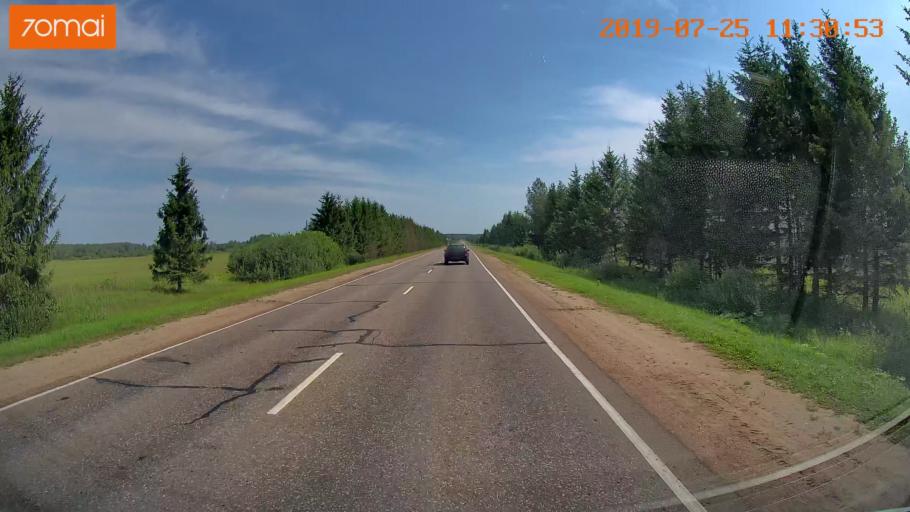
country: RU
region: Ivanovo
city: Privolzhsk
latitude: 57.3871
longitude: 41.3337
